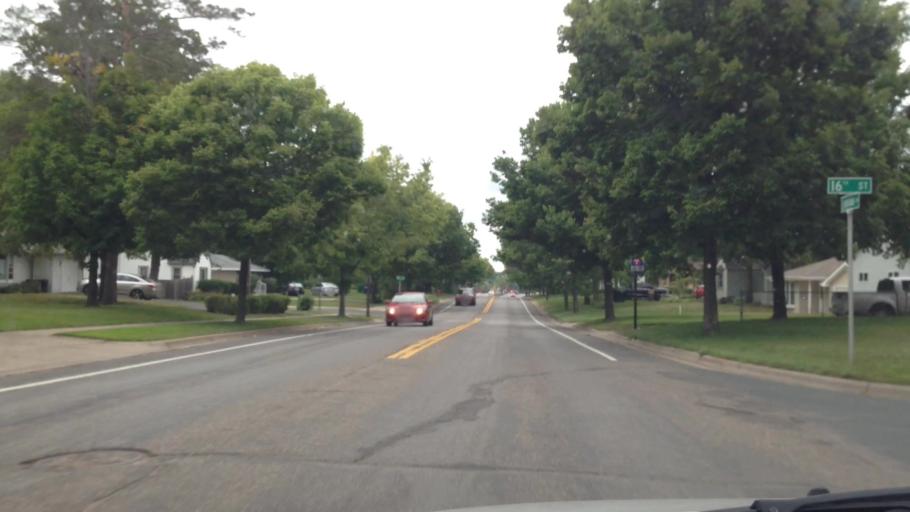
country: US
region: Minnesota
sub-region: Hennepin County
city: Saint Louis Park
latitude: 44.9669
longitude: -93.3709
